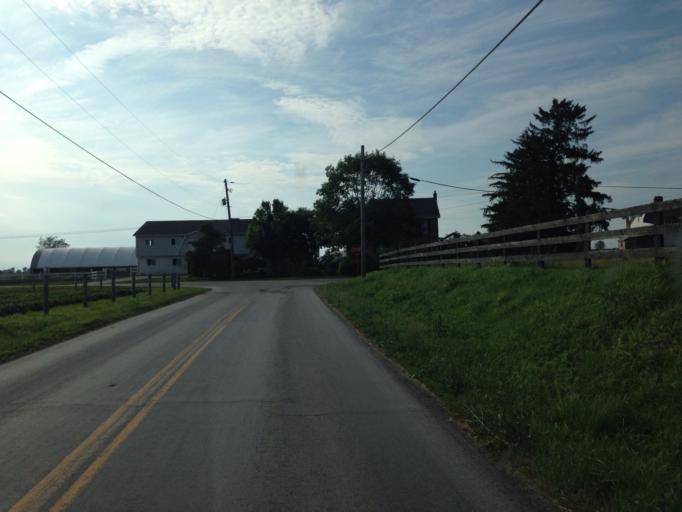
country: US
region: Pennsylvania
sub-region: Lancaster County
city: Brownstown
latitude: 40.0552
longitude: -76.1956
